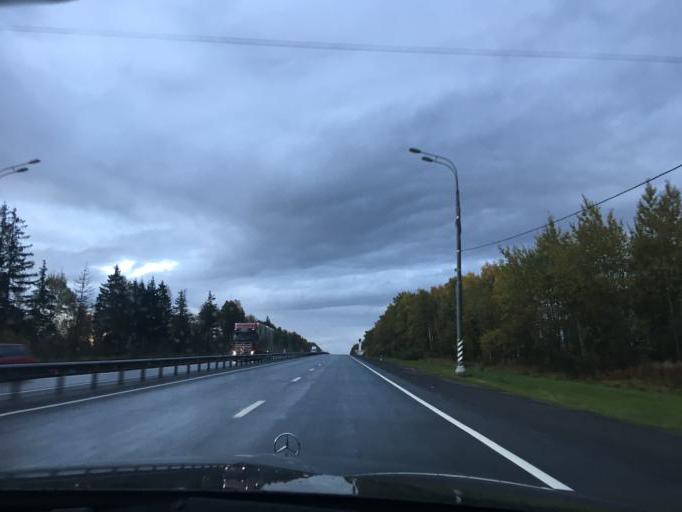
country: RU
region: Smolensk
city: Safonovo
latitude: 55.1305
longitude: 33.1765
